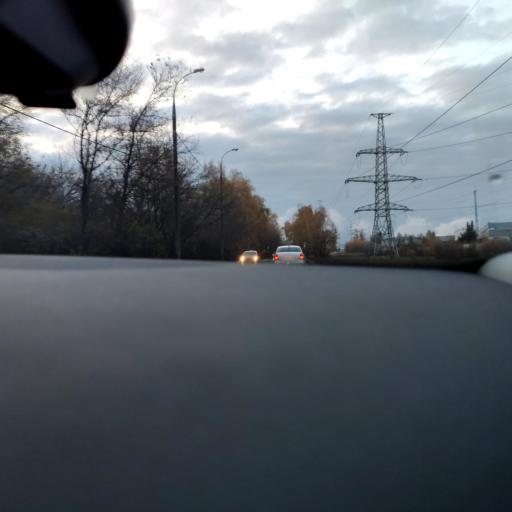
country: RU
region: Moscow
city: Kapotnya
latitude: 55.6661
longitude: 37.8080
